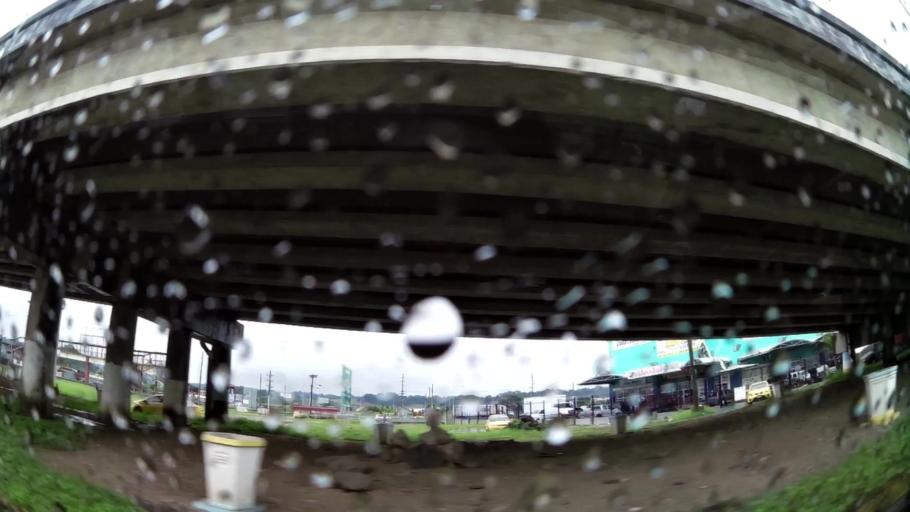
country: PA
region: Colon
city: Arco Iris
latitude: 9.3393
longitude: -79.8819
